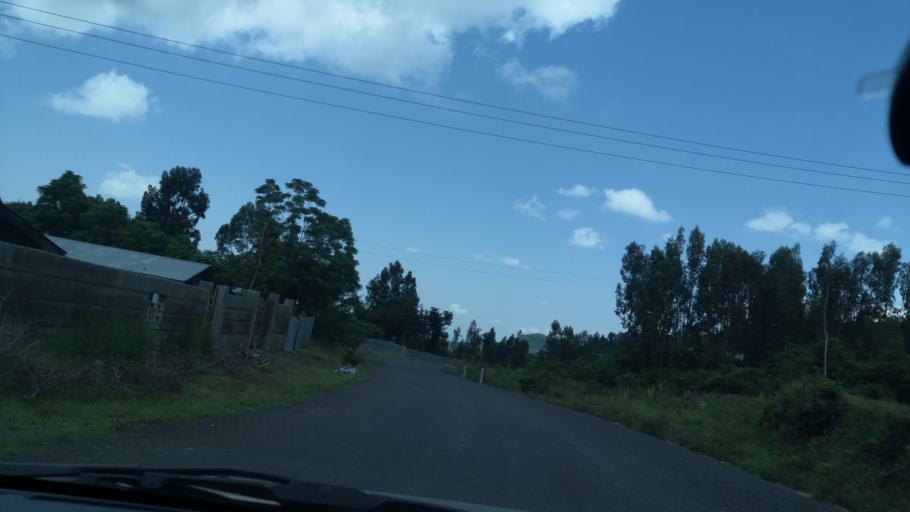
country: ET
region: Amhara
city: Abomsa
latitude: 10.3187
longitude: 39.8739
